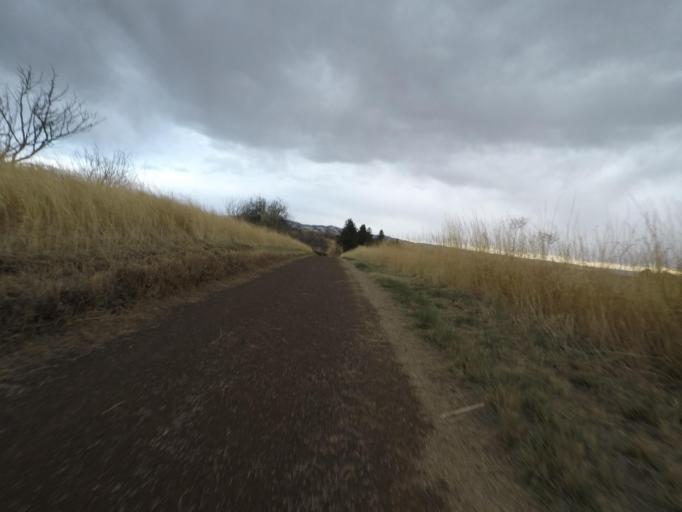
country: US
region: Washington
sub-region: Walla Walla County
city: Walla Walla East
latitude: 46.0713
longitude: -118.2575
